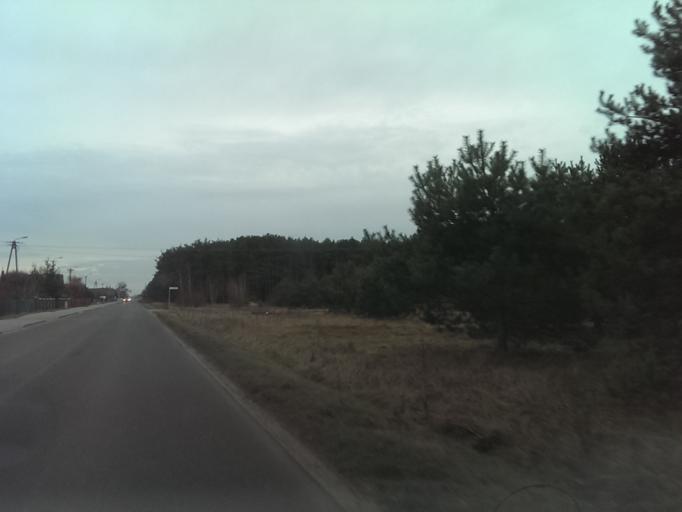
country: PL
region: Kujawsko-Pomorskie
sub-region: Powiat nakielski
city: Szubin
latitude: 53.0778
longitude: 17.7935
